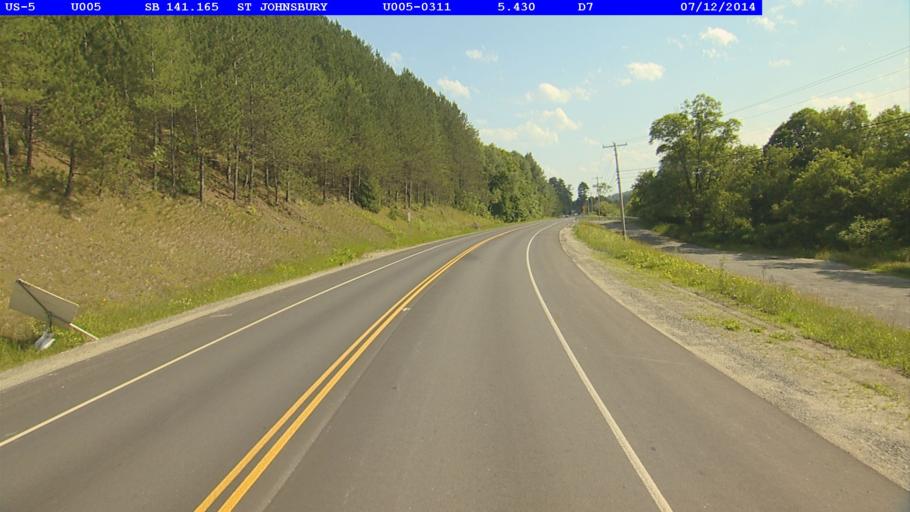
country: US
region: Vermont
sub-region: Caledonia County
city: St Johnsbury
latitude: 44.4692
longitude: -72.0133
